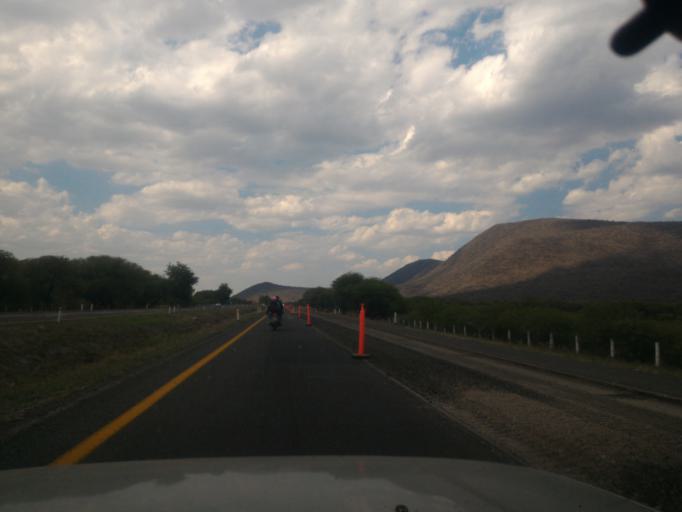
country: MX
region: Jalisco
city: Zacoalco de Torres
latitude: 20.1727
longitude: -103.5073
